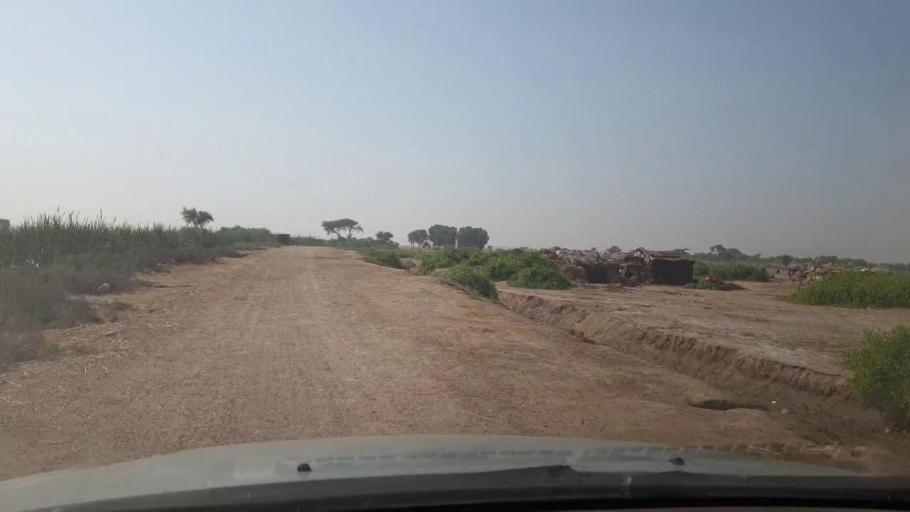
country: PK
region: Sindh
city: Bulri
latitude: 24.9071
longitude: 68.4345
